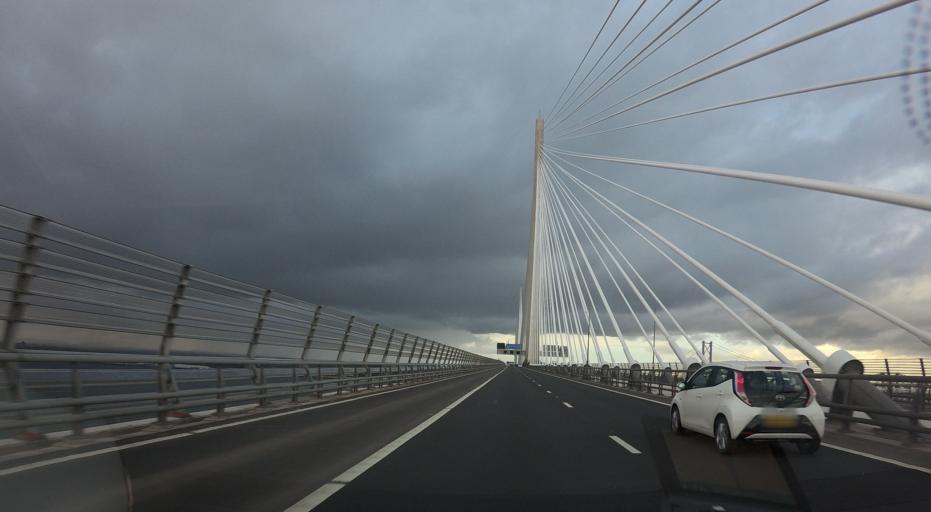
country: GB
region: Scotland
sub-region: Edinburgh
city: Queensferry
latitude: 55.9970
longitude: -3.4177
